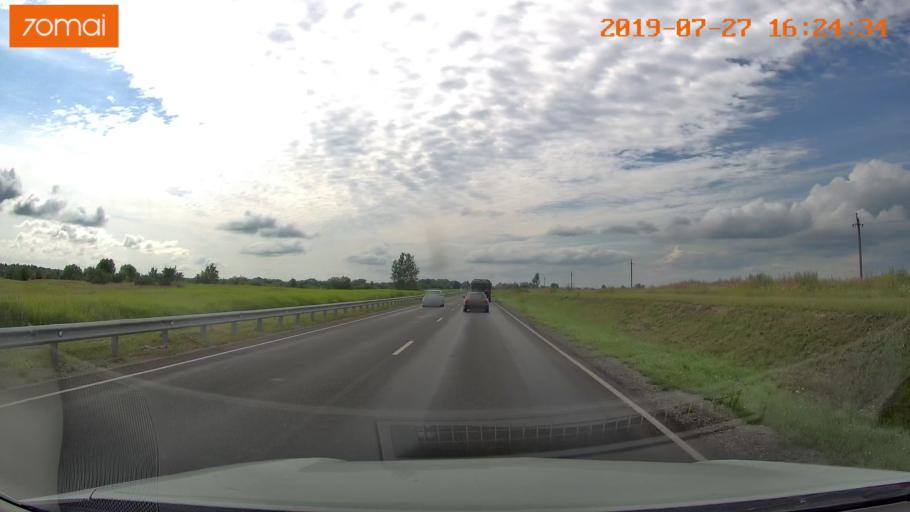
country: RU
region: Kaliningrad
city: Zheleznodorozhnyy
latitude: 54.6345
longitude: 21.4496
